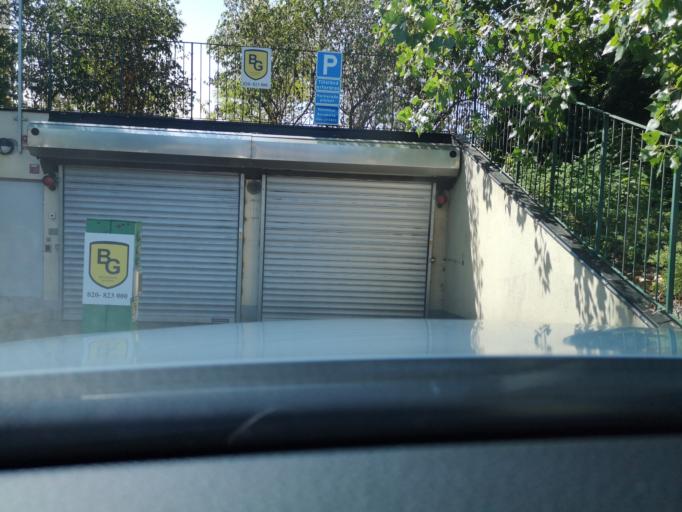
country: SE
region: Skane
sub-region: Malmo
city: Malmoe
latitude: 55.5898
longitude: 13.0394
